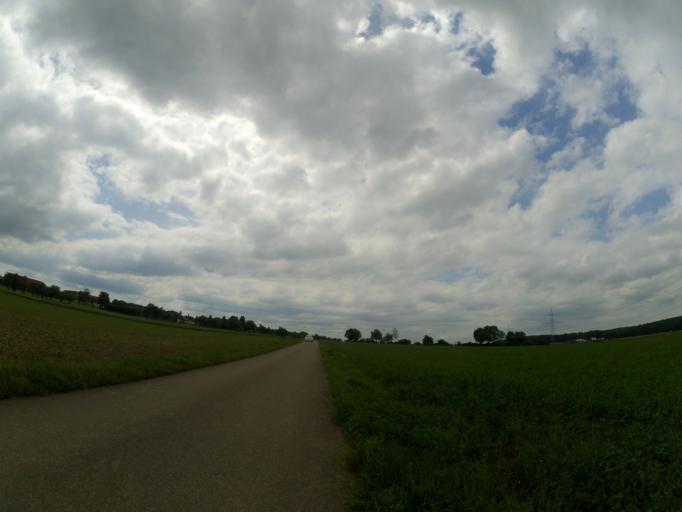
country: DE
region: Baden-Wuerttemberg
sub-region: Tuebingen Region
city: Blaubeuren
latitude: 48.4201
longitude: 9.8153
